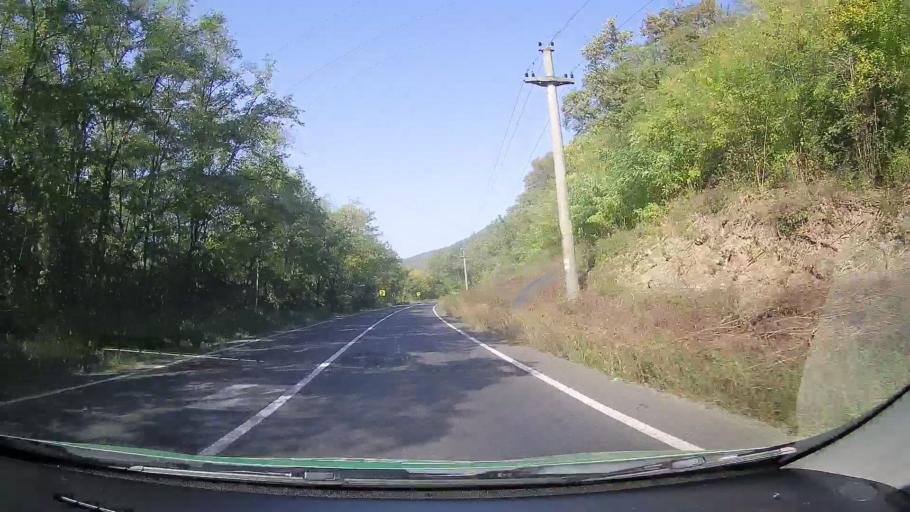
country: RO
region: Arad
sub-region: Comuna Savarsin
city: Savarsin
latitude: 46.0036
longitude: 22.2771
